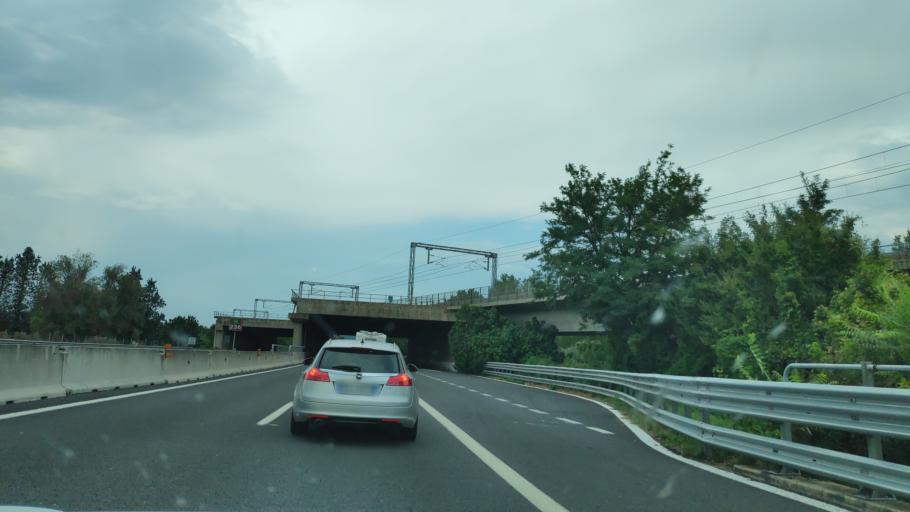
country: IT
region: Tuscany
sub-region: Province of Florence
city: Figline Valdarno
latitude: 43.6396
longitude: 11.4660
